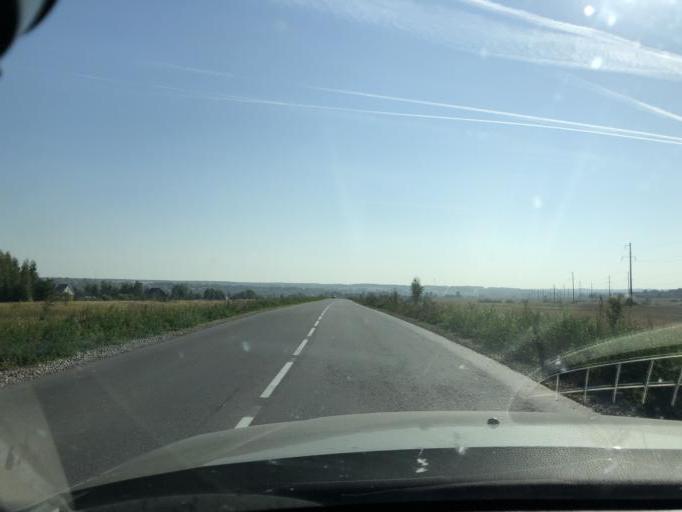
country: RU
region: Tula
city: Yasnogorsk
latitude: 54.4694
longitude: 37.6654
